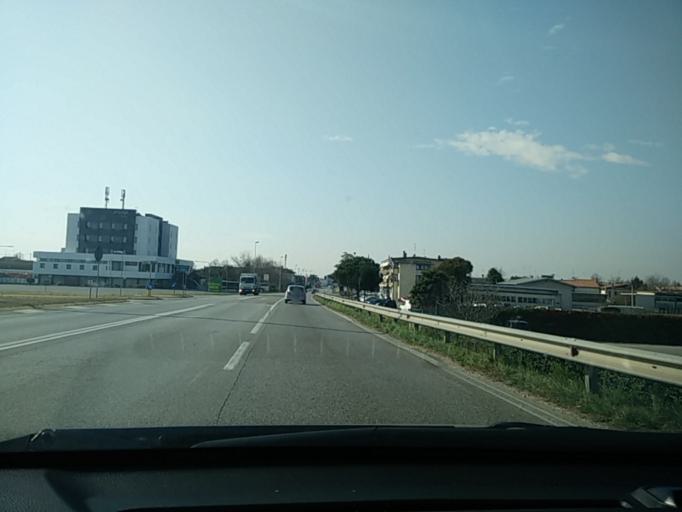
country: IT
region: Veneto
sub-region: Provincia di Treviso
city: San Vendemiano-Fossamerlo
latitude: 45.8937
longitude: 12.3285
